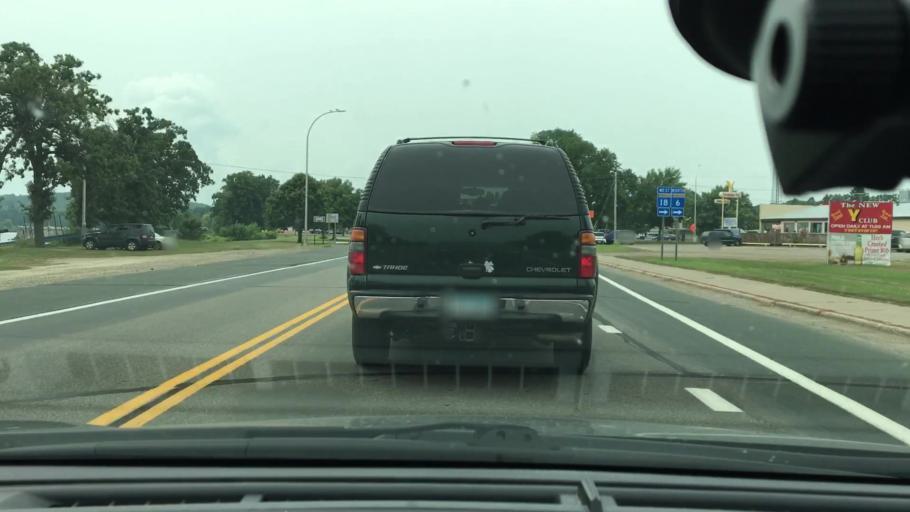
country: US
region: Minnesota
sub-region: Mille Lacs County
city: Vineland
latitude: 46.2965
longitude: -93.8233
